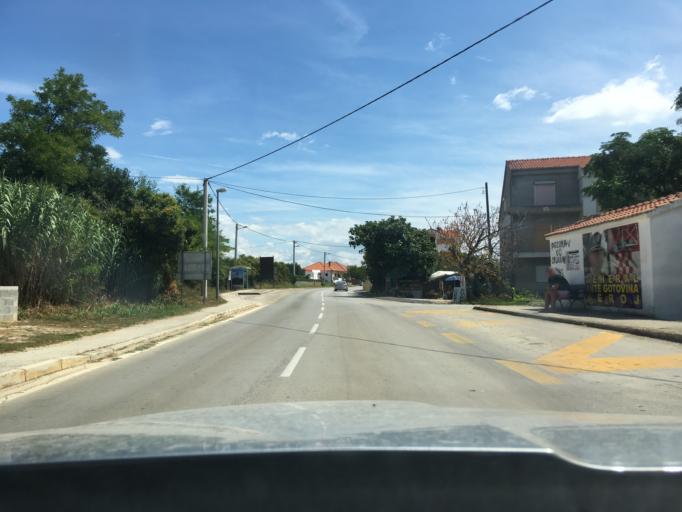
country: HR
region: Zadarska
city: Nin
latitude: 44.2473
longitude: 15.1528
